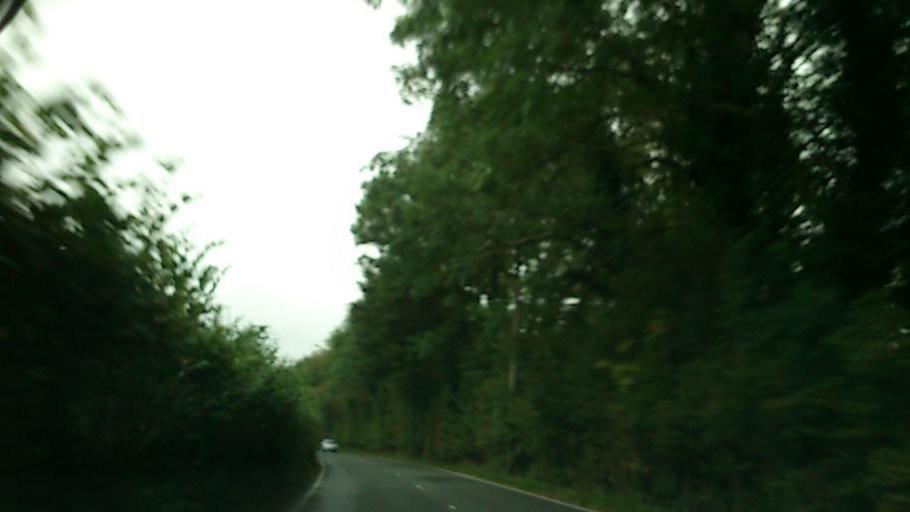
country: GB
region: Wales
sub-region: Gwynedd
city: Corris
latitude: 52.7009
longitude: -3.6597
